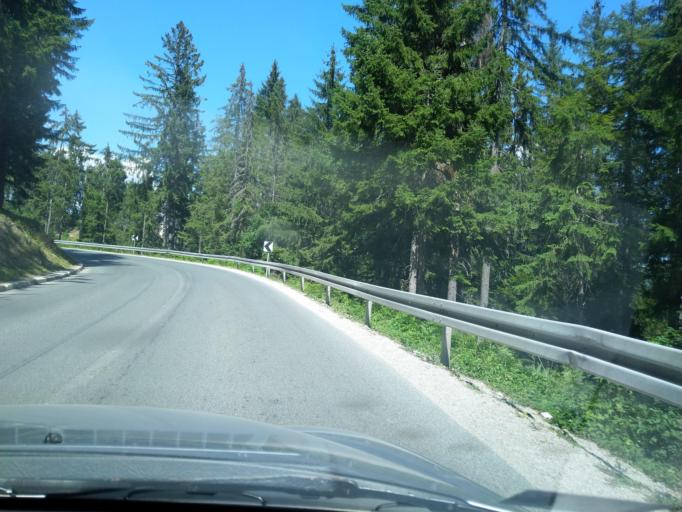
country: RS
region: Central Serbia
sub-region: Zlatiborski Okrug
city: Nova Varos
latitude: 43.4446
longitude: 19.8211
